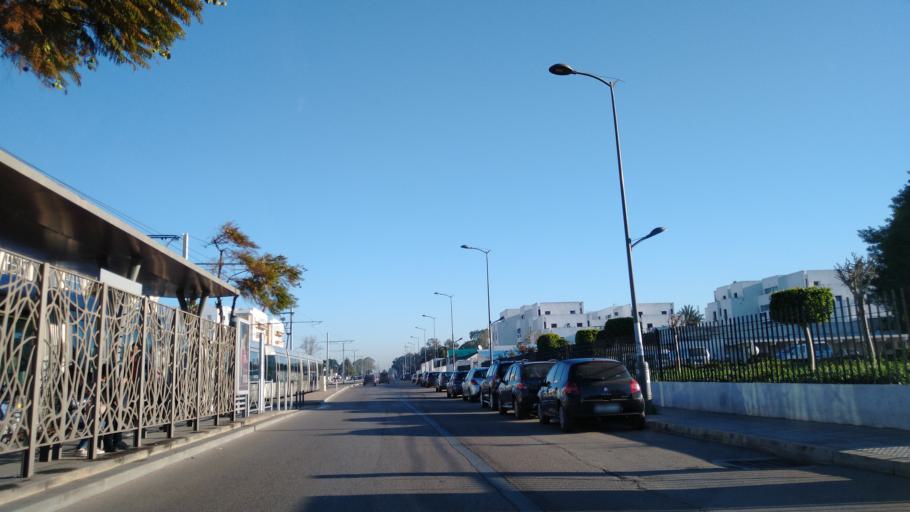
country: MA
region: Rabat-Sale-Zemmour-Zaer
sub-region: Rabat
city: Rabat
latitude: 33.9826
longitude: -6.8641
